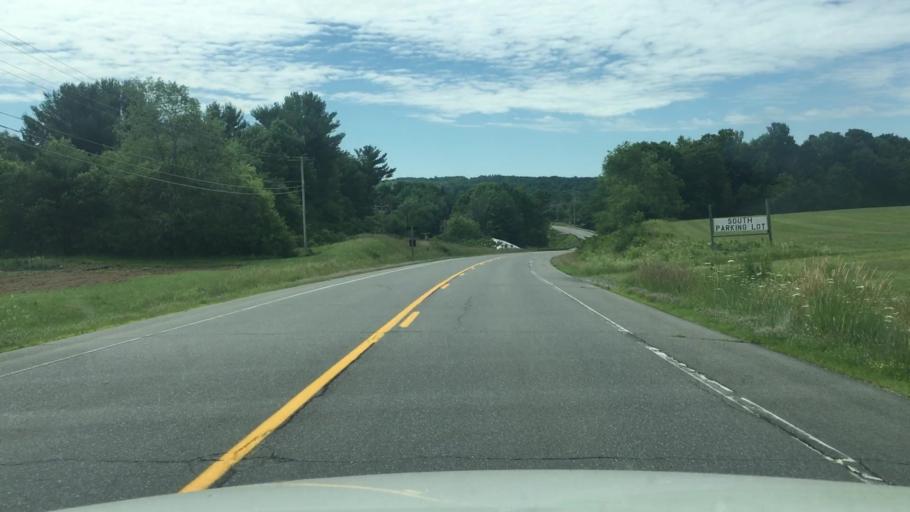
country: US
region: Maine
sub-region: Waldo County
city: Troy
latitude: 44.5848
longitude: -69.2797
